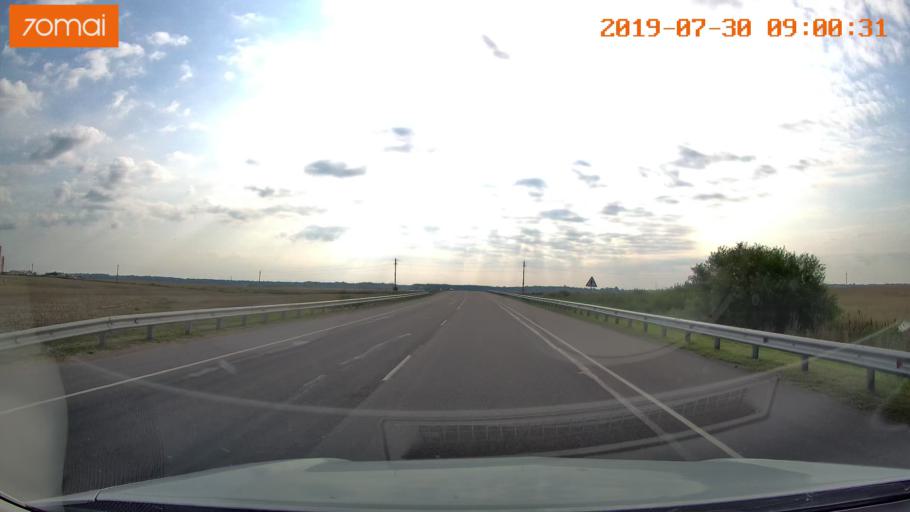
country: RU
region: Kaliningrad
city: Gusev
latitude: 54.6145
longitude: 22.1838
